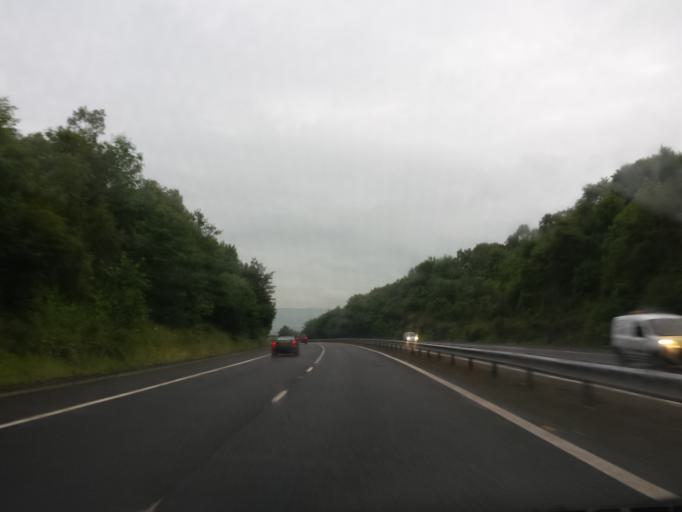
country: GB
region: Scotland
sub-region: Perth and Kinross
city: Perth
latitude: 56.3743
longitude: -3.4453
